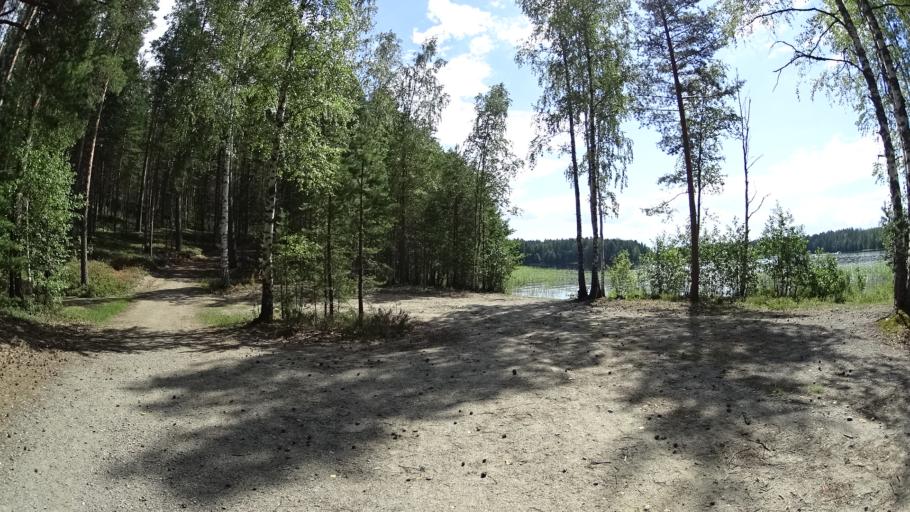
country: FI
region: Southern Savonia
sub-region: Savonlinna
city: Punkaharju
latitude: 61.7925
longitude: 29.3033
